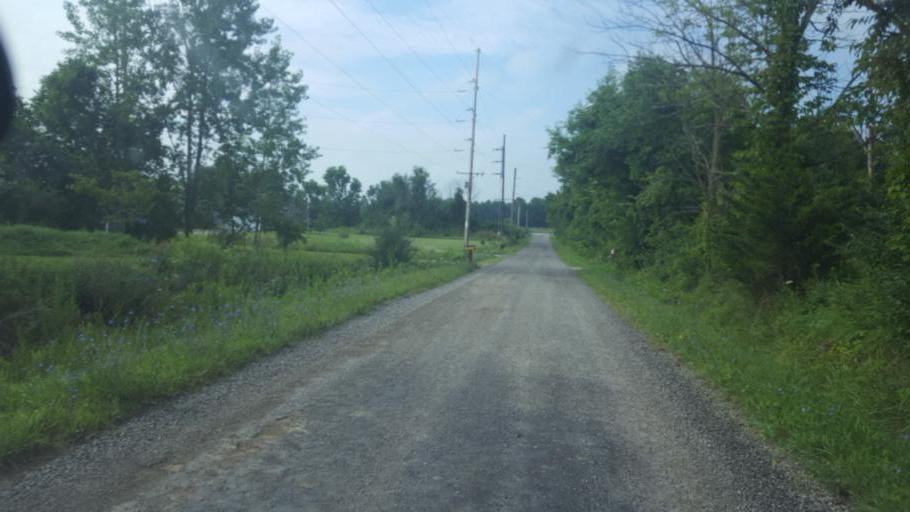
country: US
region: Ohio
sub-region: Delaware County
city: Ashley
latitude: 40.3691
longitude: -82.9116
